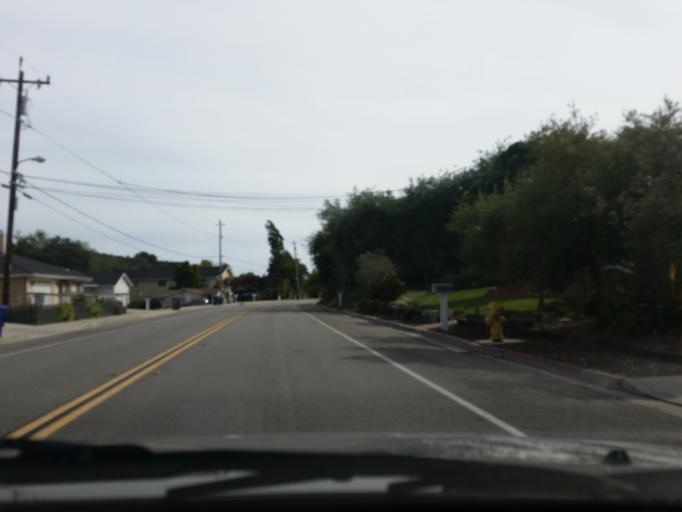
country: US
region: California
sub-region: San Luis Obispo County
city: Arroyo Grande
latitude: 35.1329
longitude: -120.5715
